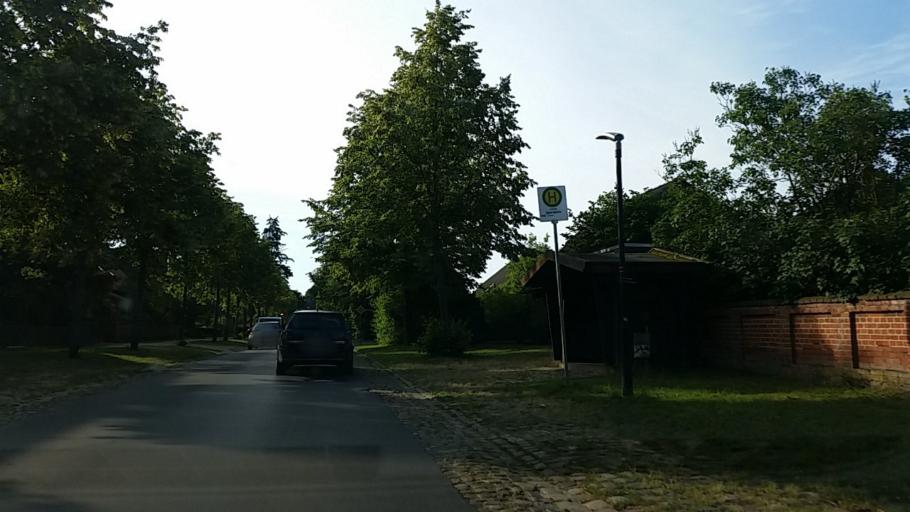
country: DE
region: Lower Saxony
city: Wieren
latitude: 52.9256
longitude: 10.6450
